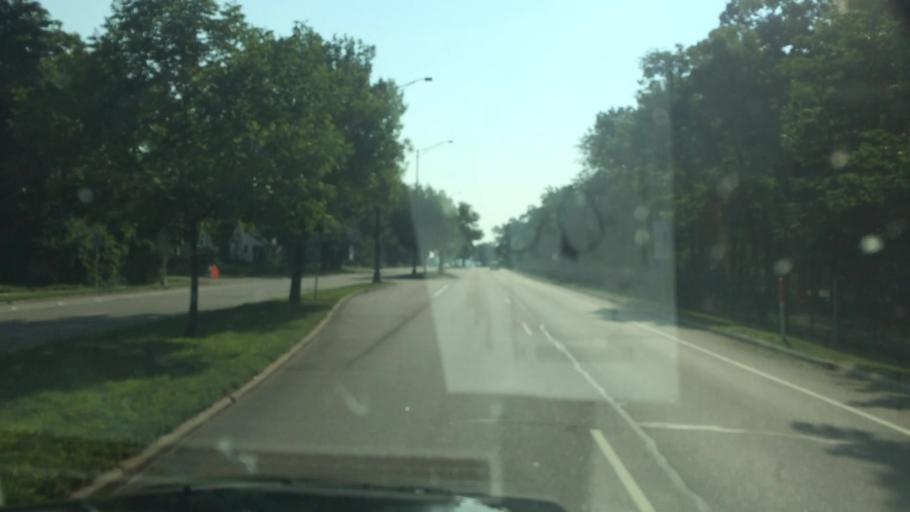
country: US
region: Wisconsin
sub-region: Marathon County
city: Wausau
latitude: 44.9590
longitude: -89.6497
